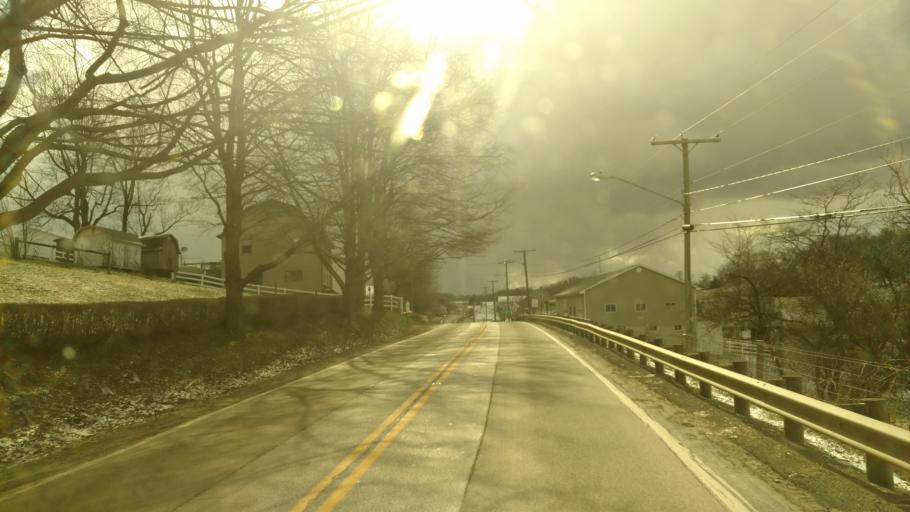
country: US
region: Ohio
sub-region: Holmes County
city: Millersburg
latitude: 40.5093
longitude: -81.7887
